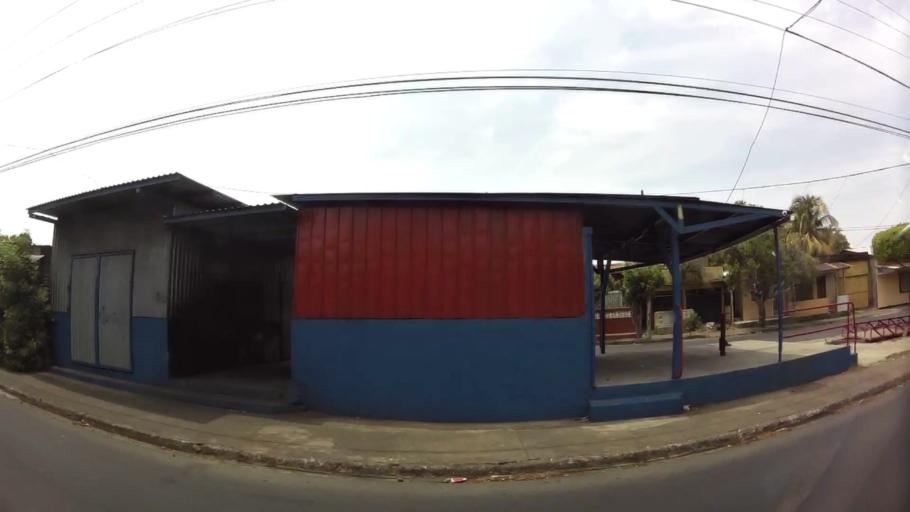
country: NI
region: Managua
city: Managua
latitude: 12.1550
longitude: -86.2946
